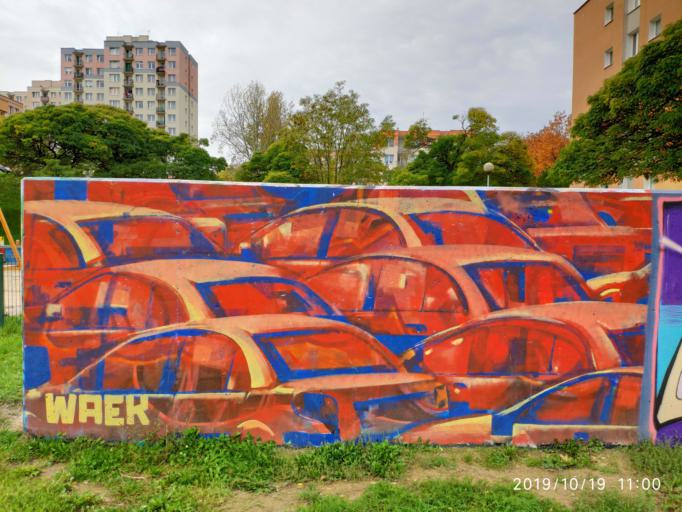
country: PL
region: Lubusz
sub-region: Zielona Gora
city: Zielona Gora
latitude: 51.9332
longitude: 15.4885
